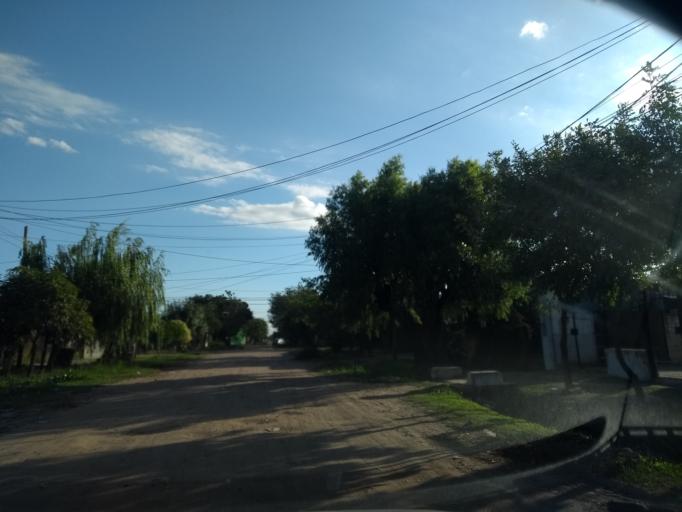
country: AR
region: Chaco
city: Barranqueras
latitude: -27.4846
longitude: -58.9397
